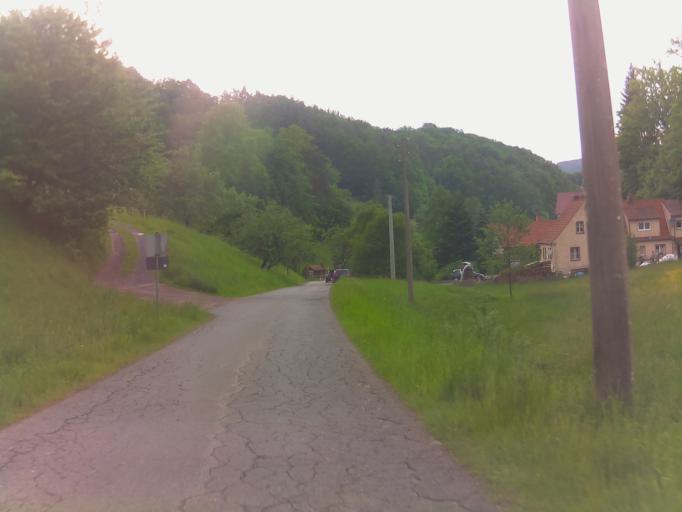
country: DE
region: Thuringia
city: Unterwellenborn
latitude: 50.7170
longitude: 11.4526
